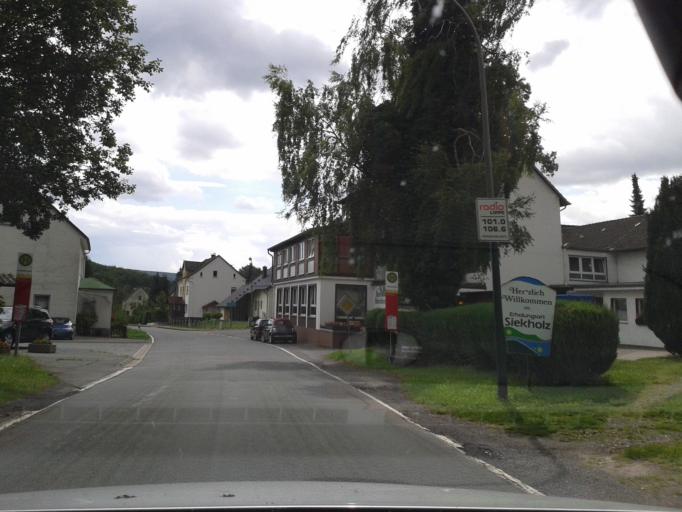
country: DE
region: North Rhine-Westphalia
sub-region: Regierungsbezirk Detmold
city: Blomberg
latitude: 51.9390
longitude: 9.1468
